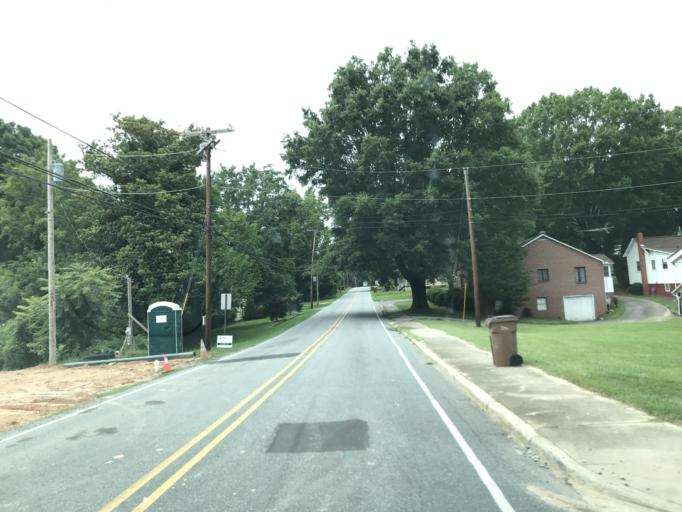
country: US
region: North Carolina
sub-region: Lincoln County
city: Lincolnton
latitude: 35.4773
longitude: -81.2496
